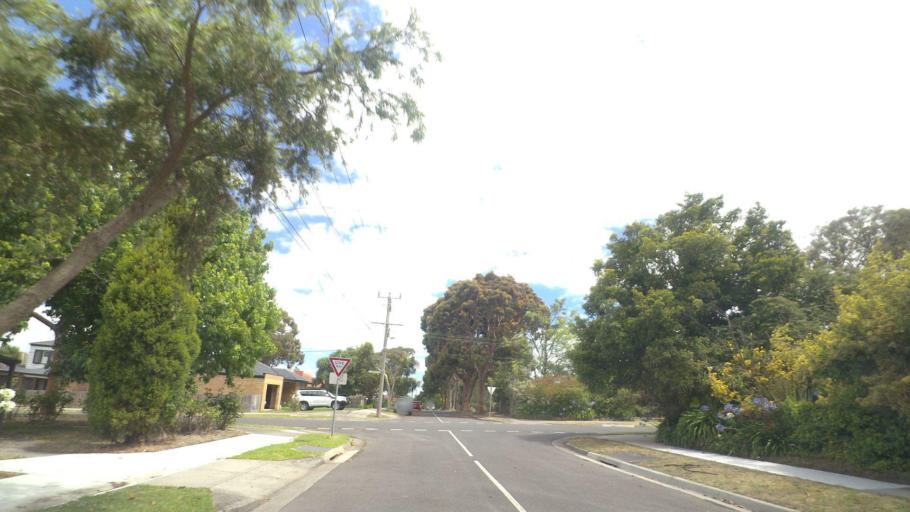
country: AU
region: Victoria
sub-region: Knox
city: Bayswater
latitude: -37.8599
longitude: 145.2442
